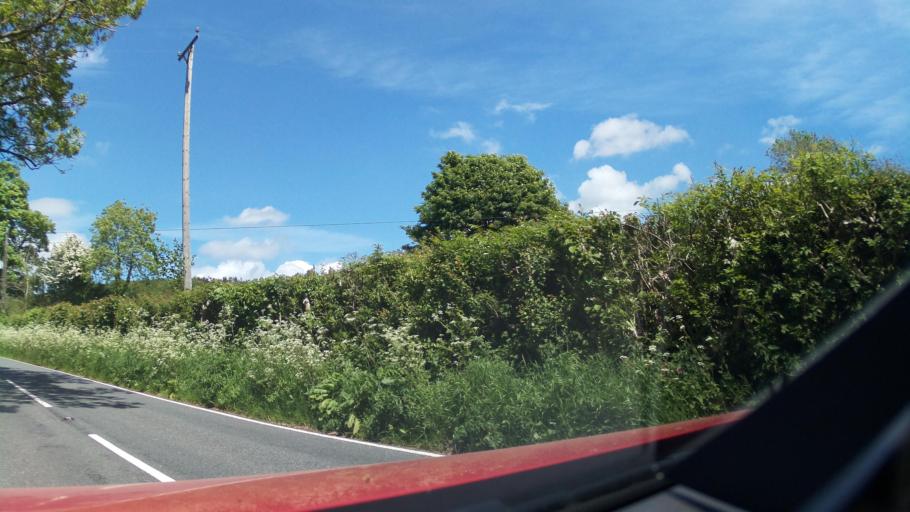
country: GB
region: Wales
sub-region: Monmouthshire
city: Mitchel Troy
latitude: 51.7542
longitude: -2.7219
